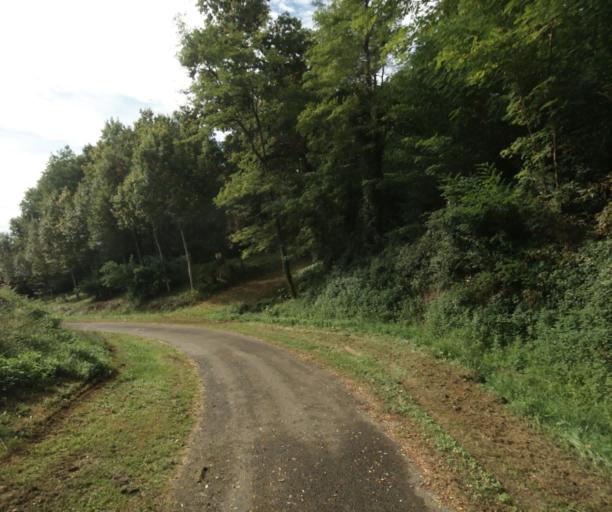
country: FR
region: Aquitaine
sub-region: Departement des Landes
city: Villeneuve-de-Marsan
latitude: 43.8922
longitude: -0.2003
